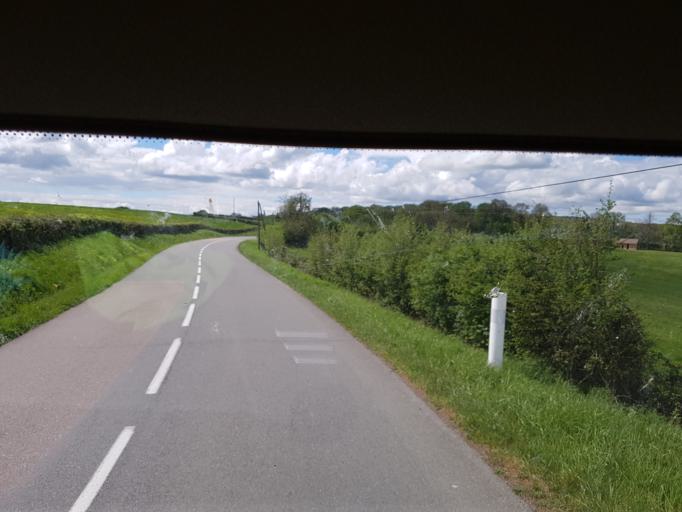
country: FR
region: Bourgogne
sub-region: Departement de Saone-et-Loire
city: Toulon-sur-Arroux
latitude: 46.6695
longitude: 4.1885
